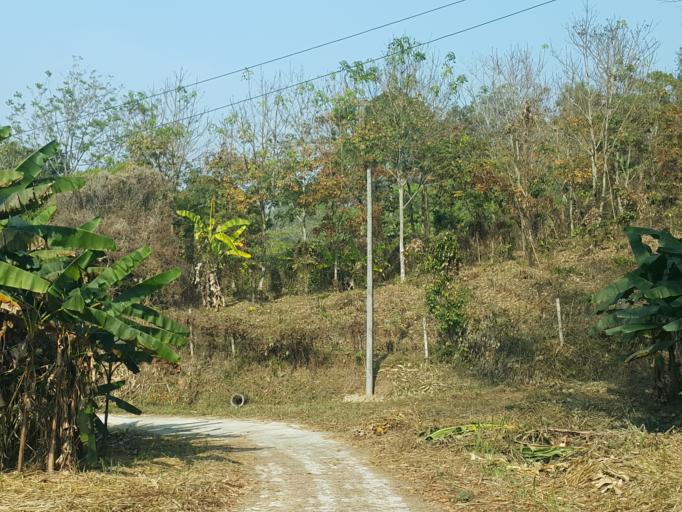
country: TH
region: Chiang Mai
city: Samoeng
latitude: 19.0136
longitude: 98.7589
